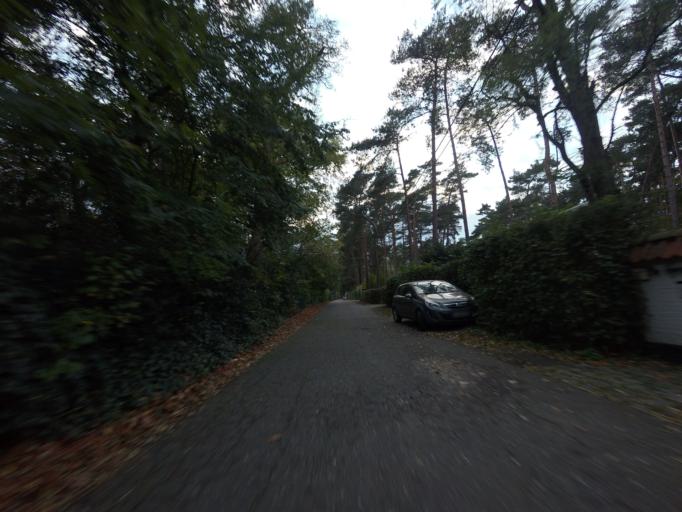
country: BE
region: Flanders
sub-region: Provincie Antwerpen
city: Bonheiden
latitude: 51.0159
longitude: 4.5812
